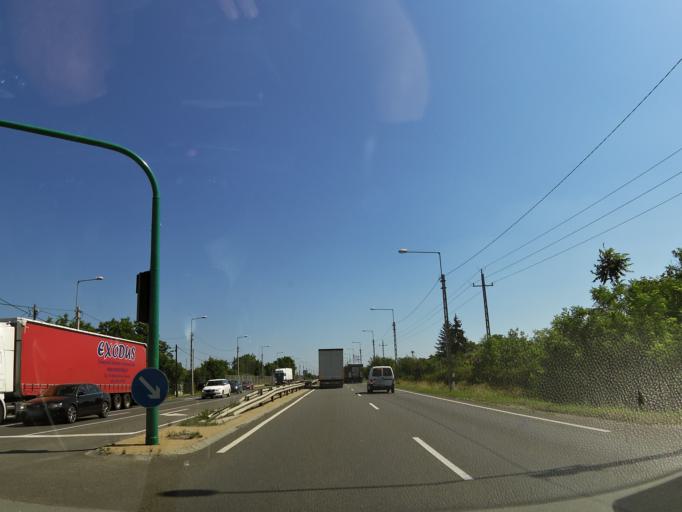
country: HU
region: Jasz-Nagykun-Szolnok
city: Torokszentmiklos
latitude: 47.2051
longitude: 20.4782
